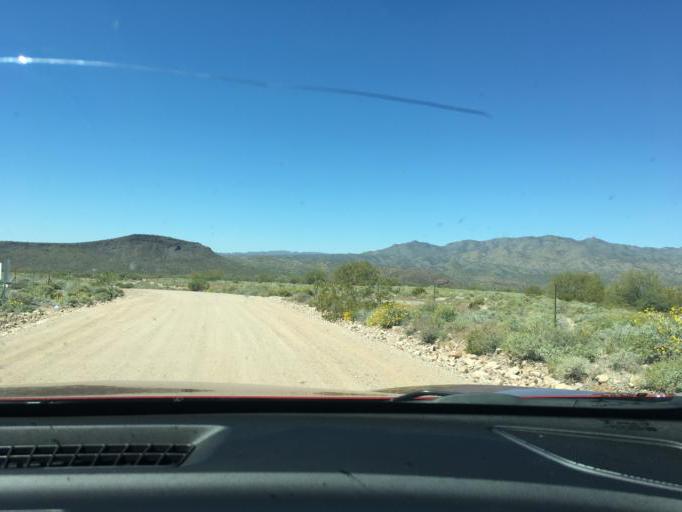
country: US
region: Arizona
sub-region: Yavapai County
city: Bagdad
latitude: 34.6112
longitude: -113.5212
